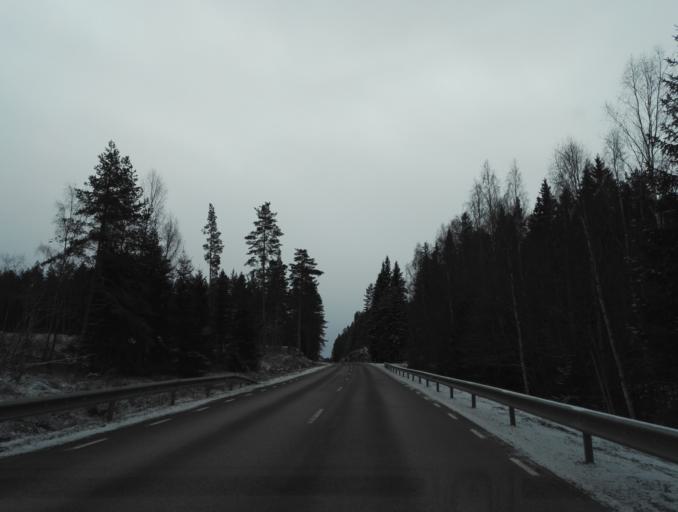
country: SE
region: Kalmar
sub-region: Hultsfreds Kommun
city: Virserum
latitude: 57.2832
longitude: 15.5668
